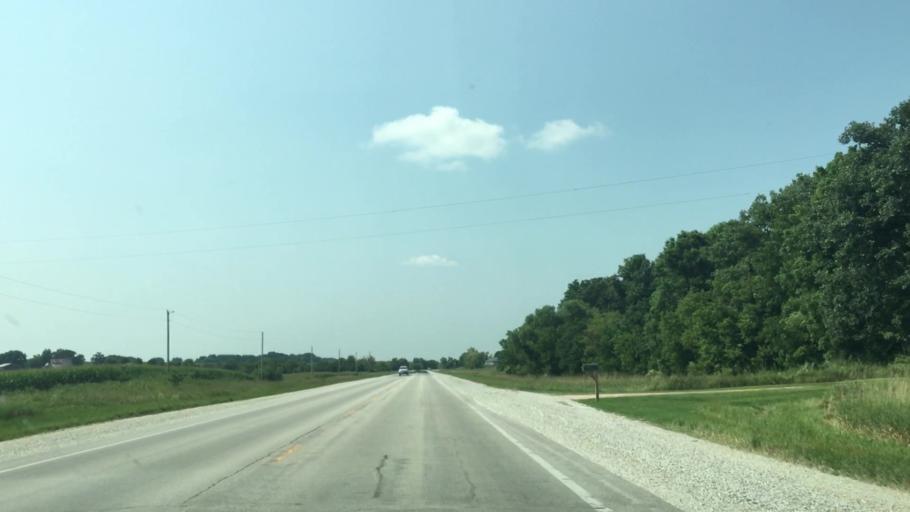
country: US
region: Iowa
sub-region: Winneshiek County
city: Decorah
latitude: 43.4011
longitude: -91.8457
